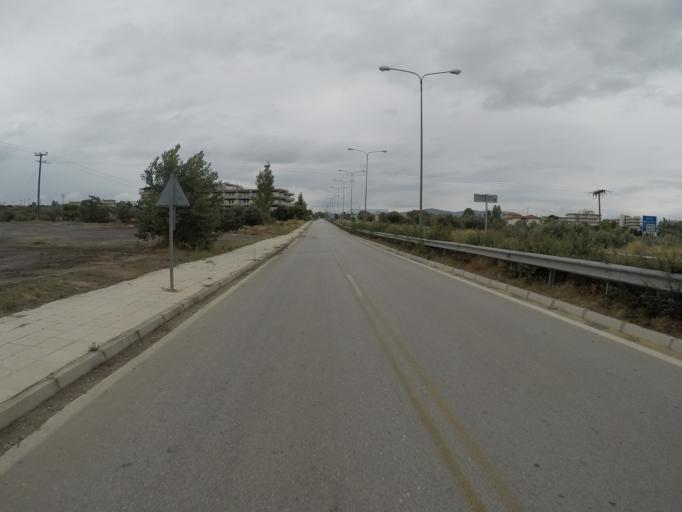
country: GR
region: Peloponnese
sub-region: Nomos Korinthias
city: Loutraki
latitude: 37.9493
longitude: 22.9794
